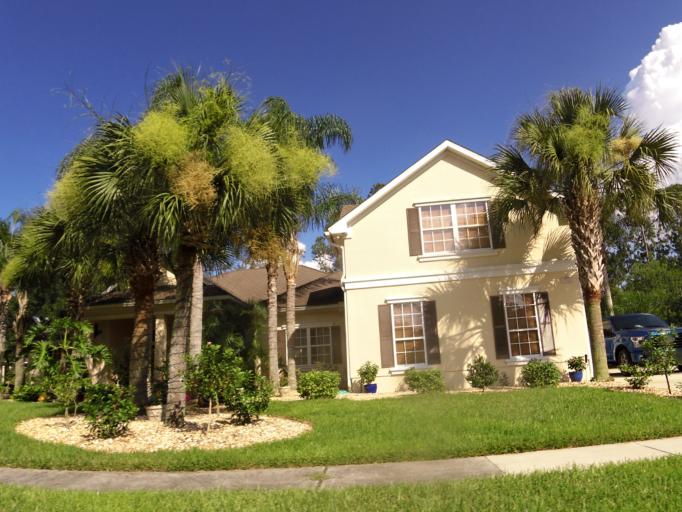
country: US
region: Florida
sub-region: Saint Johns County
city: Fruit Cove
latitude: 30.0642
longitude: -81.6492
